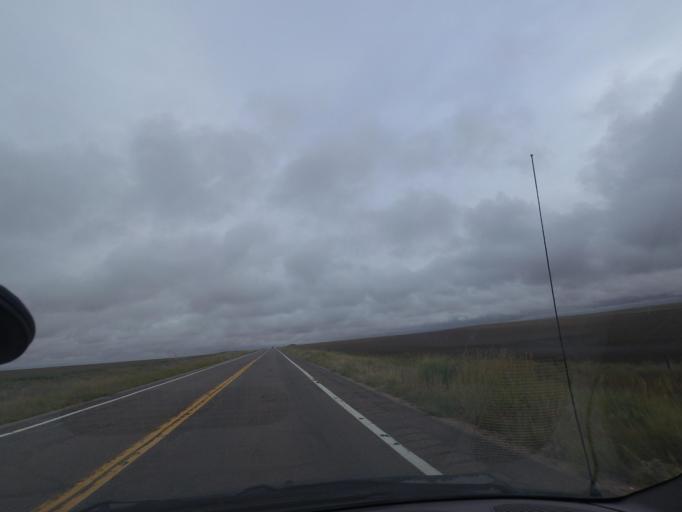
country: US
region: Colorado
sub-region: Washington County
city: Akron
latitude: 39.7385
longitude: -103.1754
